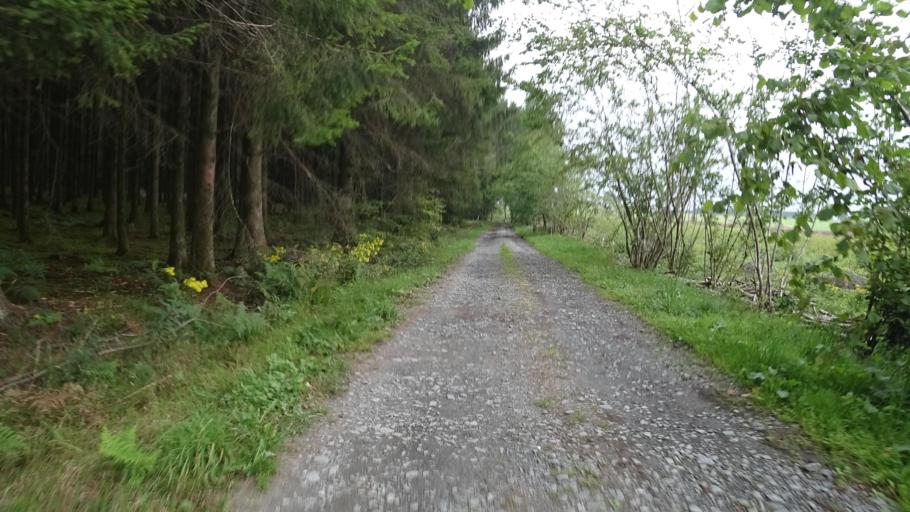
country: BE
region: Wallonia
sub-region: Province du Luxembourg
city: Chiny
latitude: 49.8016
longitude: 5.3292
